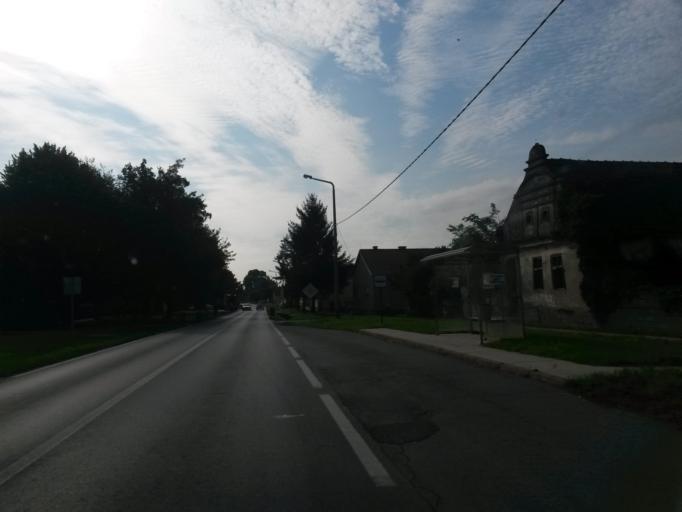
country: HR
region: Vukovarsko-Srijemska
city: Lovas
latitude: 45.2936
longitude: 19.0995
